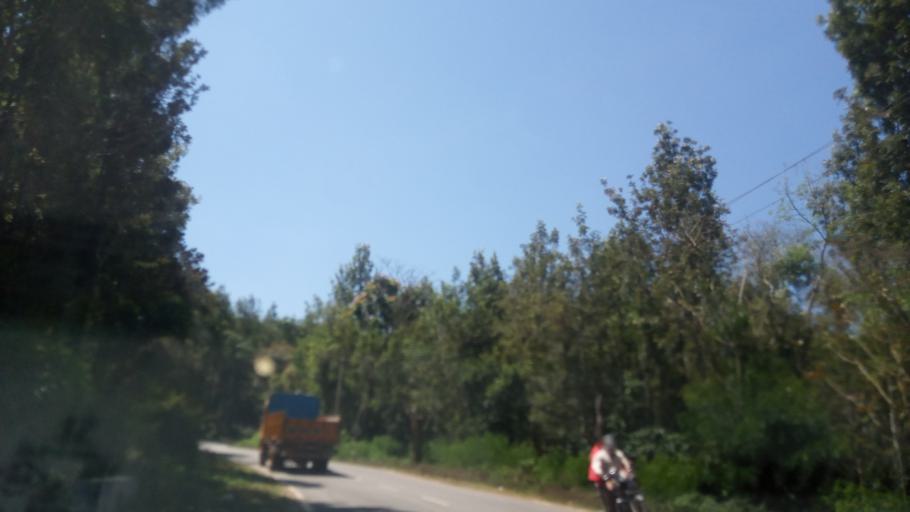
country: IN
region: Karnataka
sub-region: Chikmagalur
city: Chikmagalur
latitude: 13.3839
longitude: 75.7570
